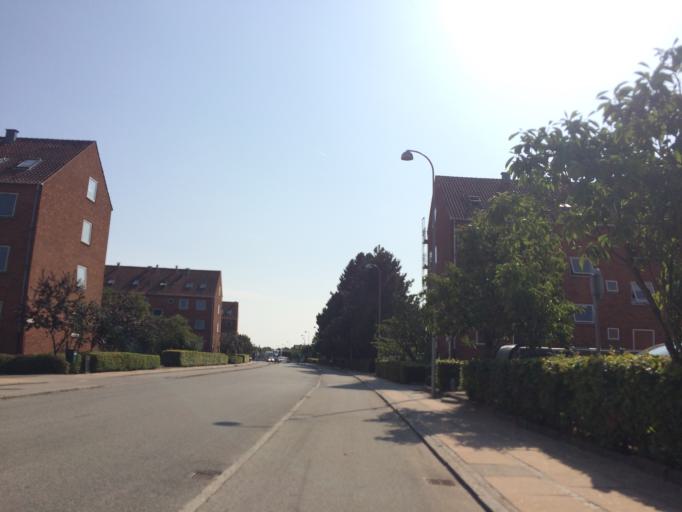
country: DK
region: Capital Region
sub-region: Hvidovre Kommune
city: Hvidovre
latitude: 55.6457
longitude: 12.4729
